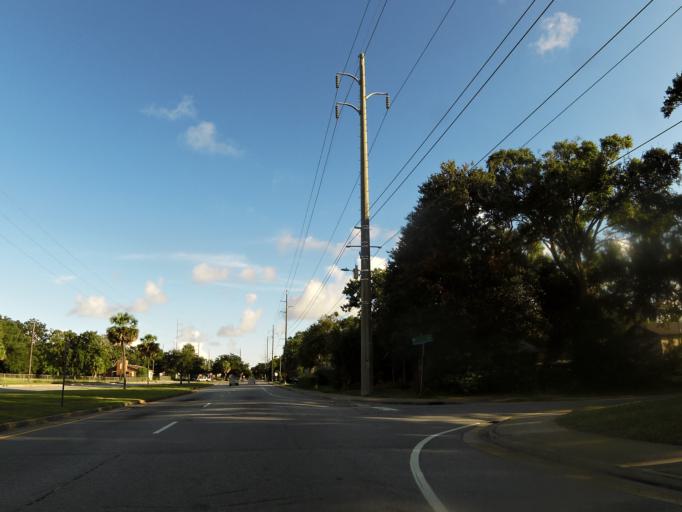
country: US
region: Georgia
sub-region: Glynn County
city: Brunswick
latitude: 31.1632
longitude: -81.4926
